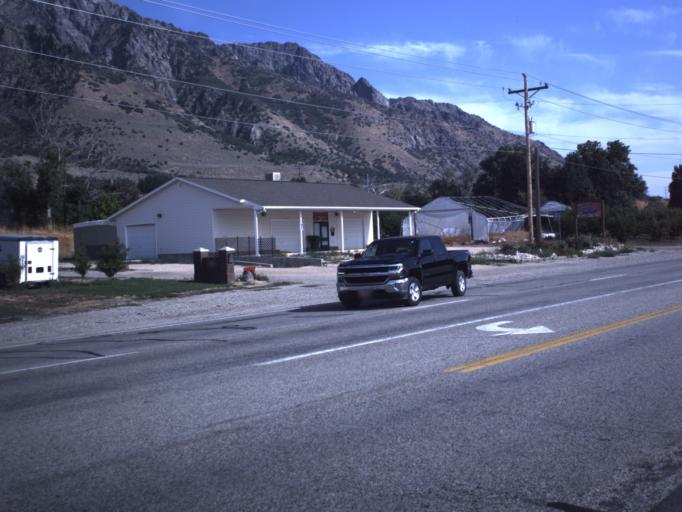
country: US
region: Utah
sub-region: Box Elder County
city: Willard
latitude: 41.4161
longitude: -112.0362
